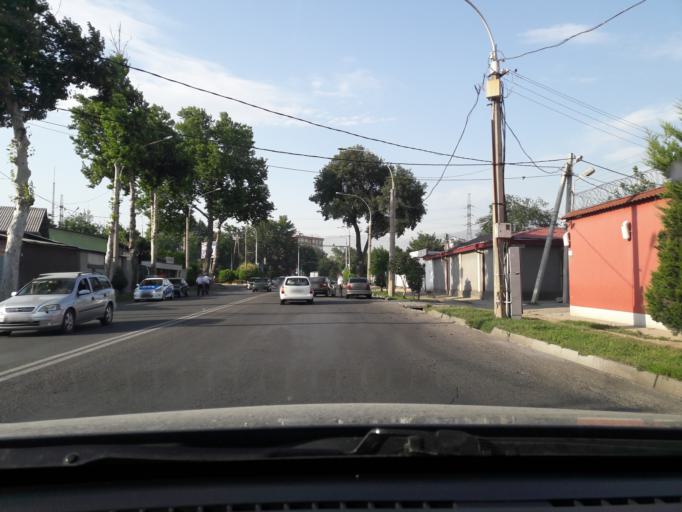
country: TJ
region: Dushanbe
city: Dushanbe
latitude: 38.5597
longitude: 68.7733
